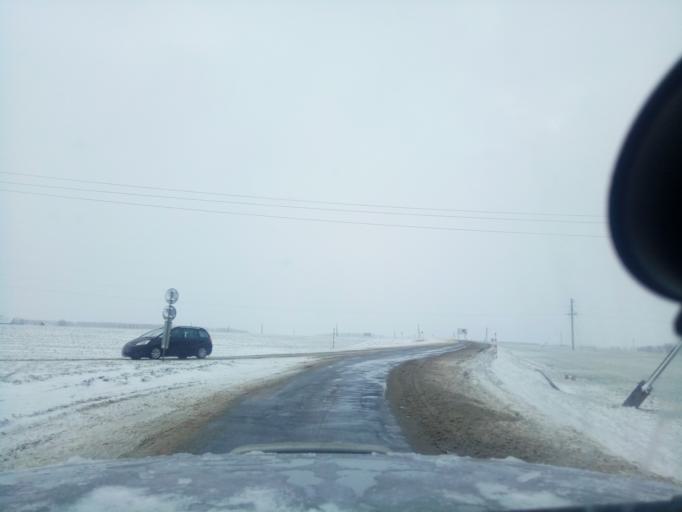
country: BY
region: Minsk
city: Haradzyeya
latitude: 53.3351
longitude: 26.5225
